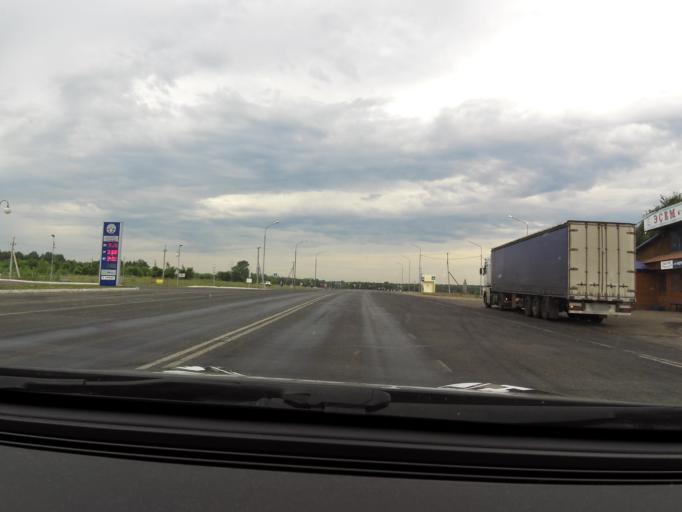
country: RU
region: Bashkortostan
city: Urman
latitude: 54.8198
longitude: 56.8789
